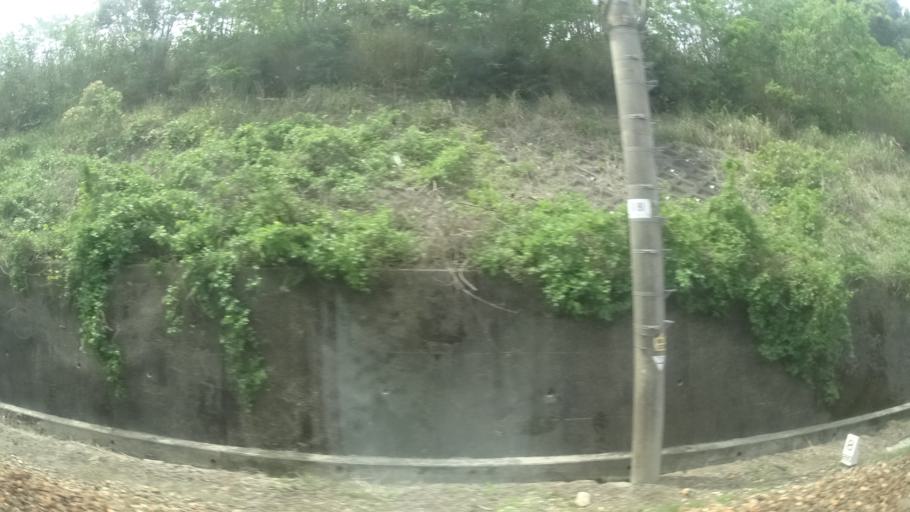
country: JP
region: Shizuoka
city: Kosai-shi
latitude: 34.7200
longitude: 137.5021
